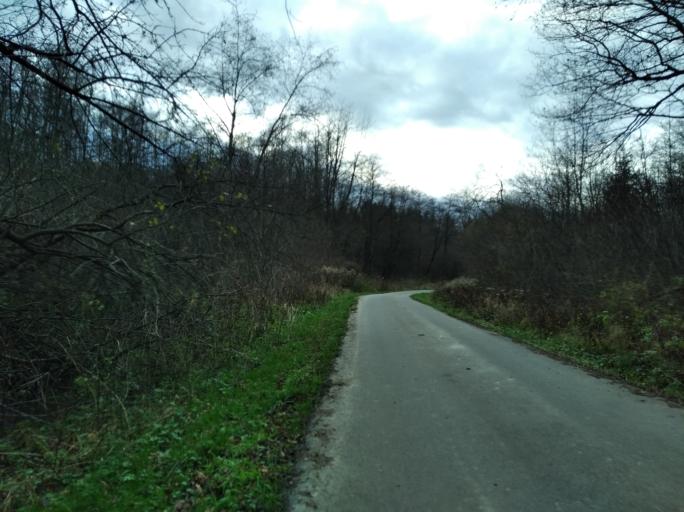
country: PL
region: Subcarpathian Voivodeship
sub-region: Powiat brzozowski
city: Domaradz
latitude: 49.7808
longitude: 21.9289
